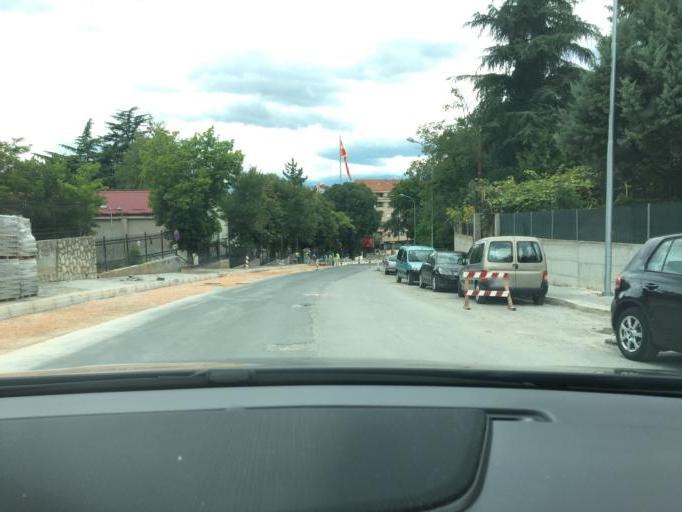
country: MK
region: Karpos
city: Skopje
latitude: 41.9868
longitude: 21.4176
